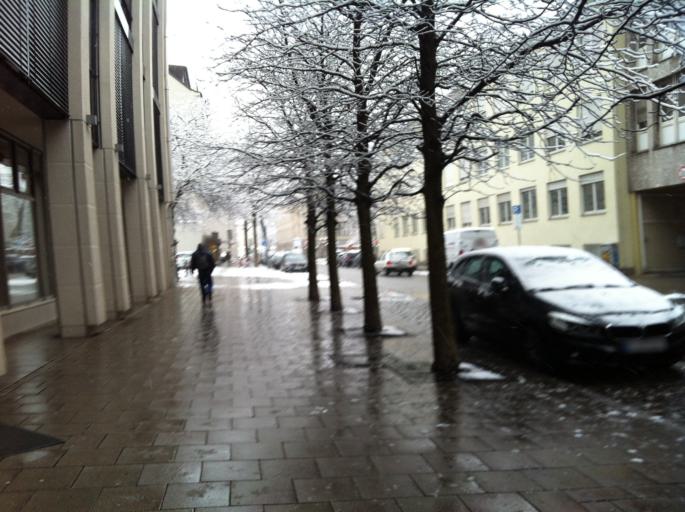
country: DE
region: Bavaria
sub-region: Upper Bavaria
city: Munich
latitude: 48.1352
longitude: 11.5608
